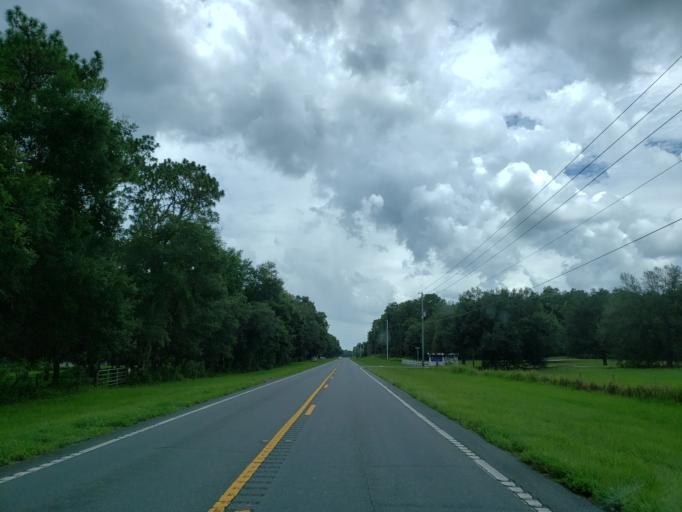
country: US
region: Florida
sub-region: Sumter County
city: Bushnell
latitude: 28.6401
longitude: -82.2288
